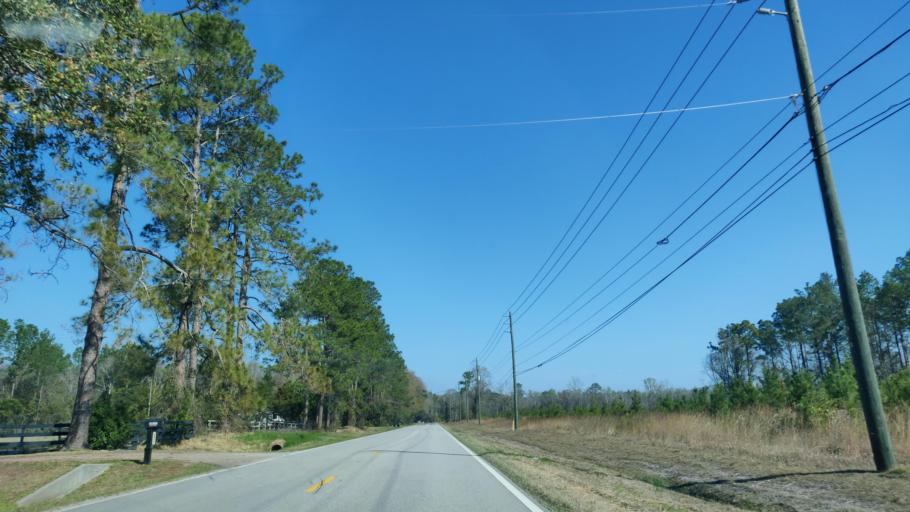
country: US
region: Florida
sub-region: Duval County
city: Baldwin
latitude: 30.2370
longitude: -81.9411
